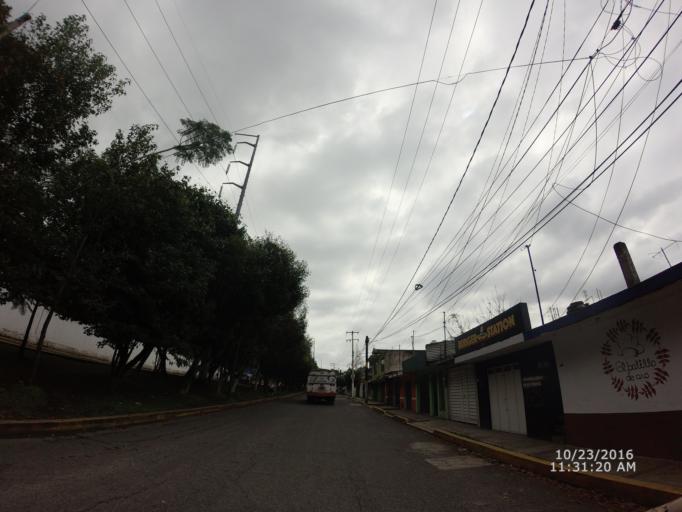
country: MX
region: Veracruz
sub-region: Tlalnelhuayocan
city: Guadalupe Victoria
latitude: 19.5493
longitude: -96.9369
